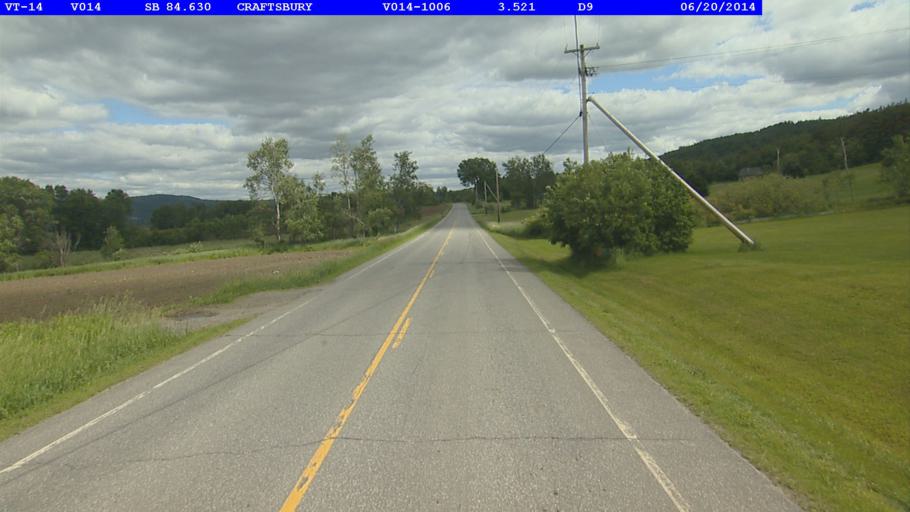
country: US
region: Vermont
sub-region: Caledonia County
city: Hardwick
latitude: 44.6420
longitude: -72.4013
